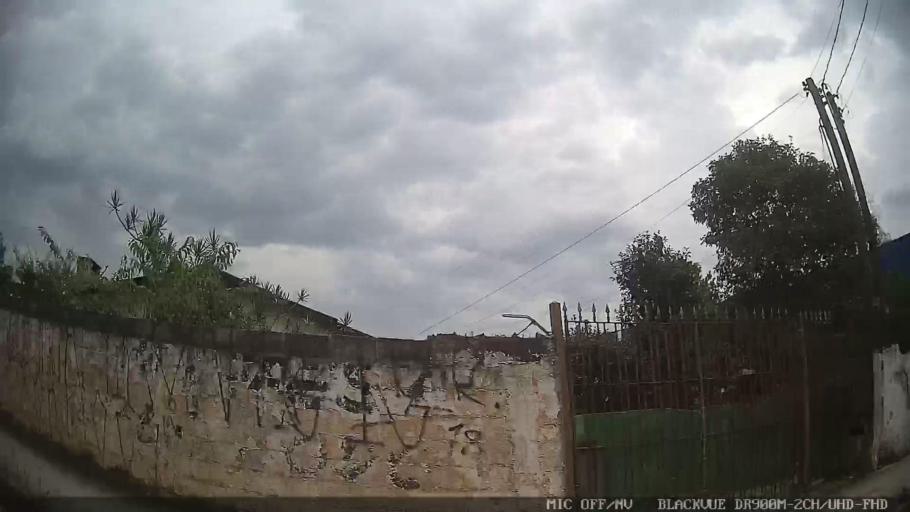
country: BR
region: Sao Paulo
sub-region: Aruja
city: Aruja
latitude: -23.4436
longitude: -46.3136
